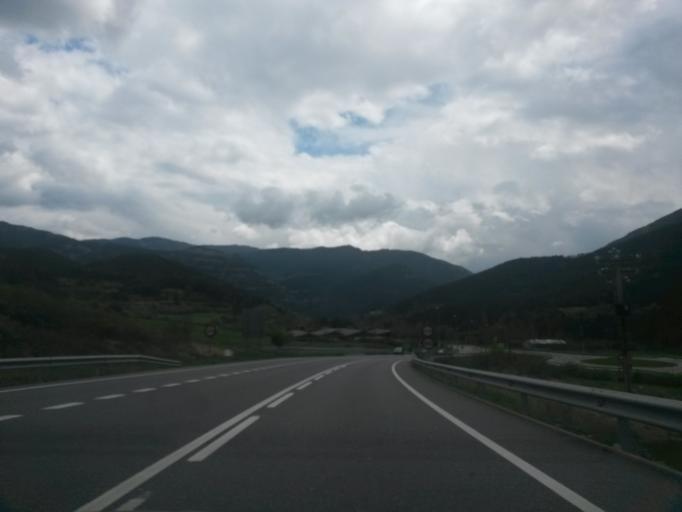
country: ES
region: Catalonia
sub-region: Provincia de Barcelona
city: Baga
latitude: 42.2487
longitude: 1.8686
